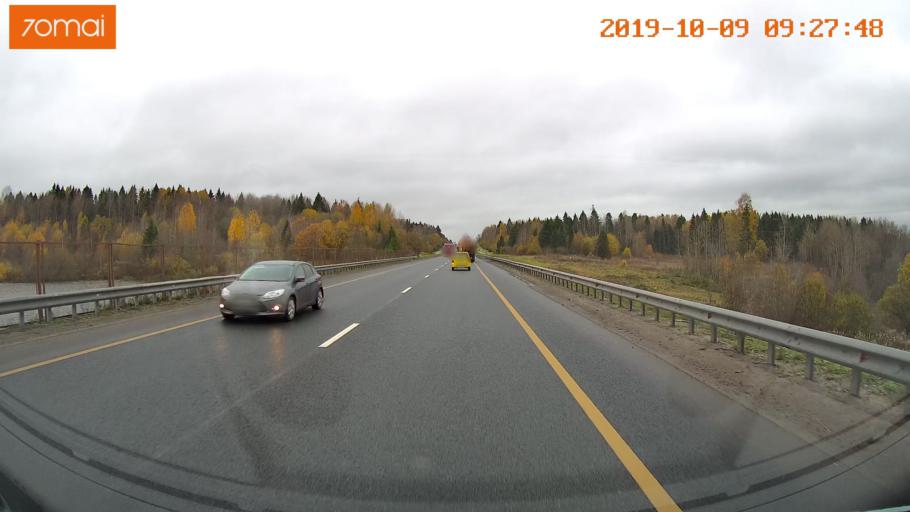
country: RU
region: Vologda
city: Vologda
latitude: 59.1167
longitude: 39.9744
